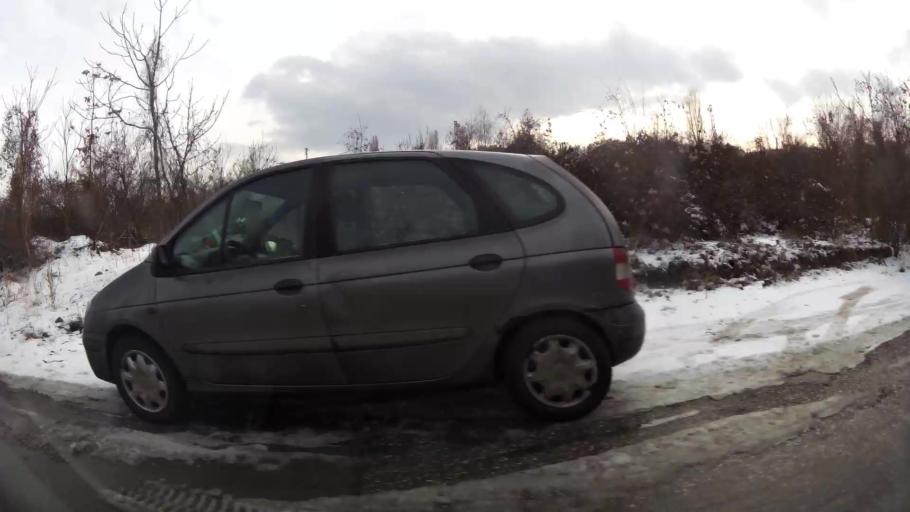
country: BG
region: Sofia-Capital
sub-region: Stolichna Obshtina
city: Sofia
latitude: 42.6975
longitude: 23.3637
